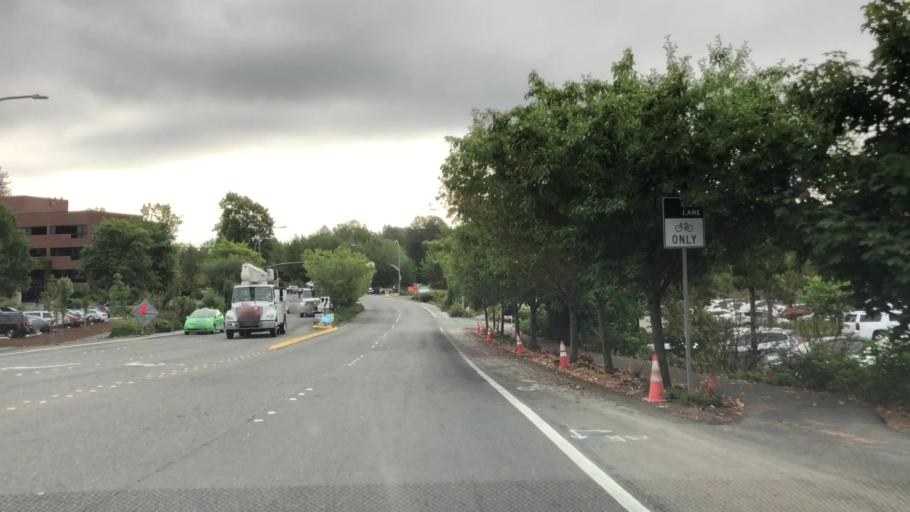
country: US
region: Washington
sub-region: King County
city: Bellevue
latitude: 47.6014
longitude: -122.1902
